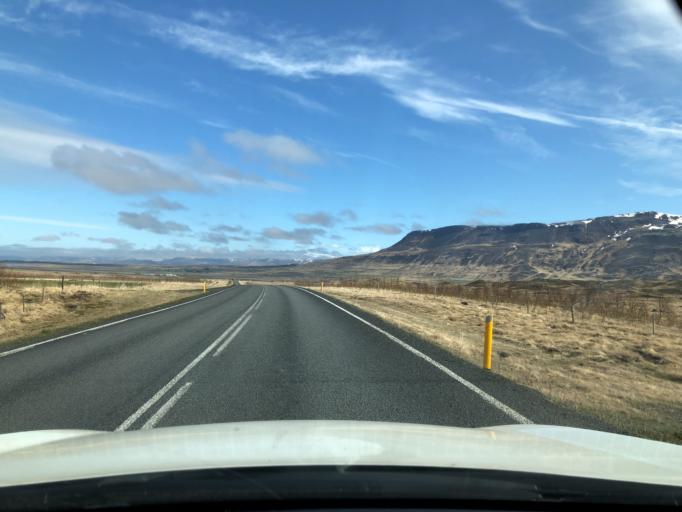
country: IS
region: Northwest
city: Saudarkrokur
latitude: 65.4948
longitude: -20.4091
